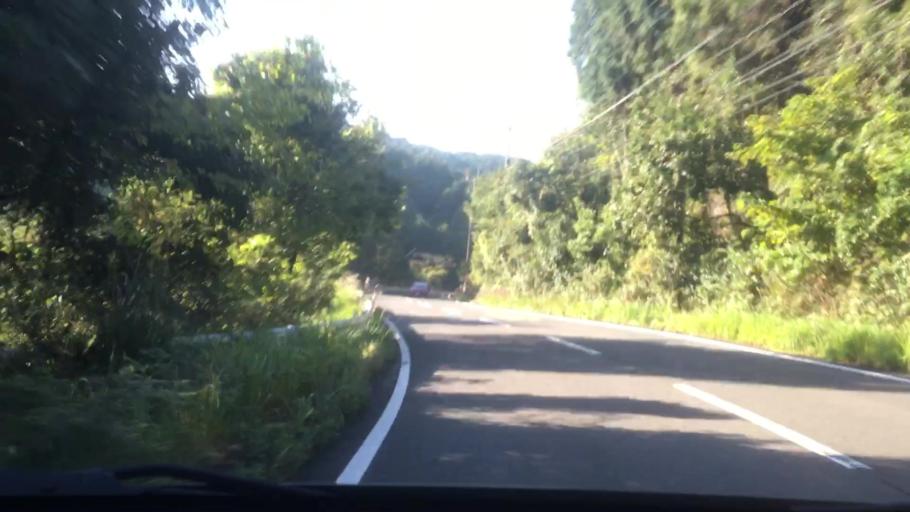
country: JP
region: Nagasaki
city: Sasebo
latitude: 32.9643
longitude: 129.6877
